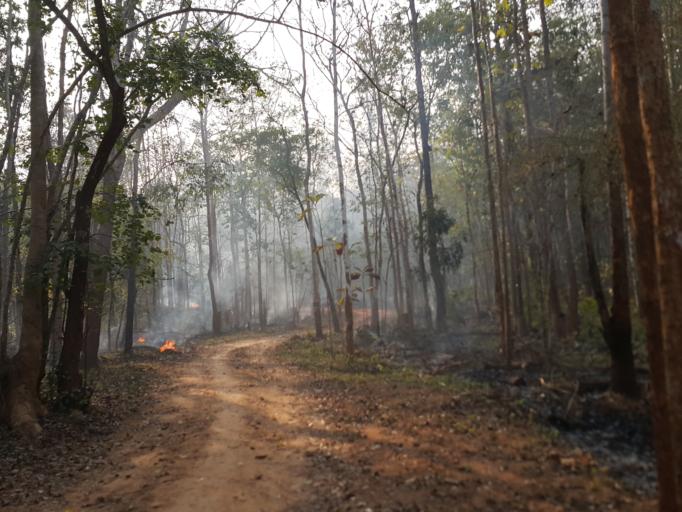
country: TH
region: Lamphun
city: Li
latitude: 17.6108
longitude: 98.9570
